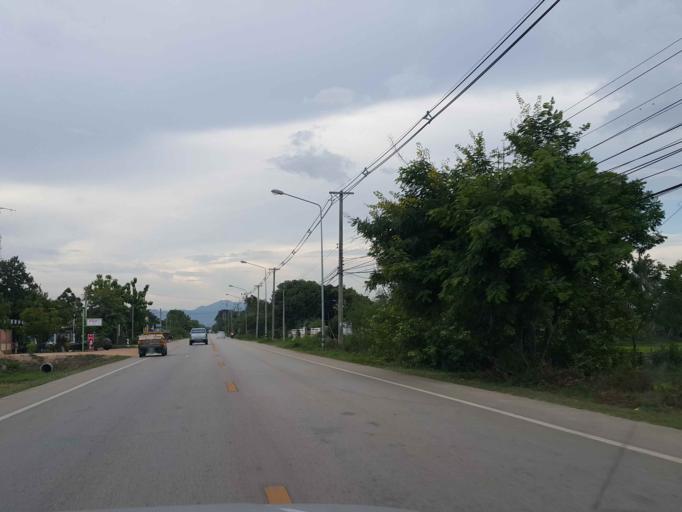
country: TH
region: Lampang
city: Hang Chat
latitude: 18.2856
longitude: 99.3793
